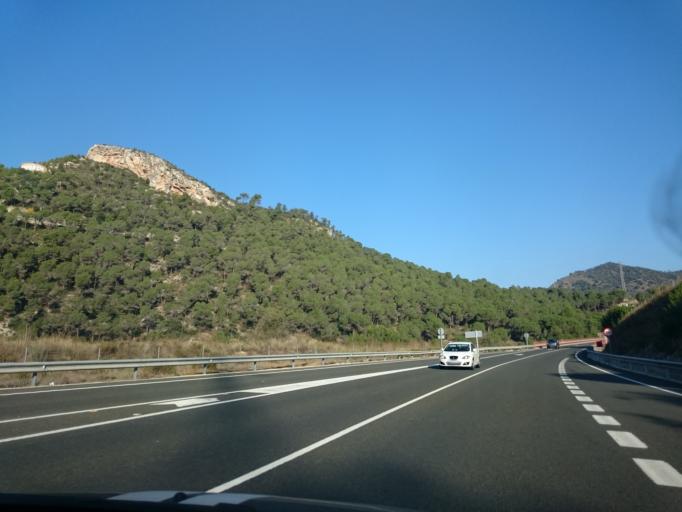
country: ES
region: Catalonia
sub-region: Provincia de Barcelona
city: Capellades
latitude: 41.5149
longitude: 1.6983
